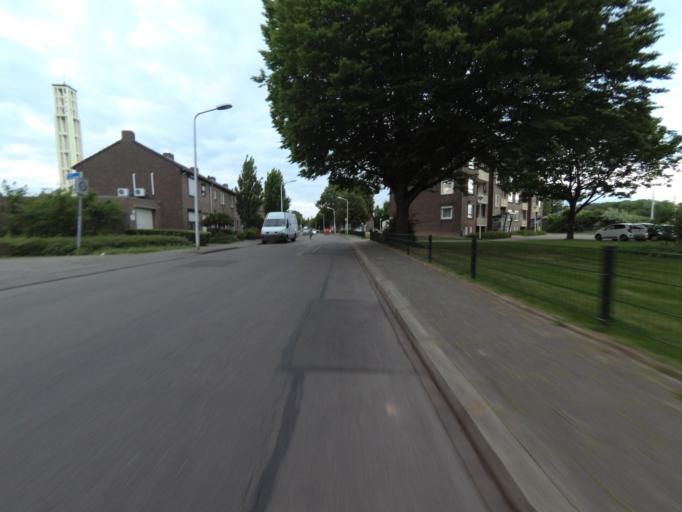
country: NL
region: Limburg
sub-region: Gemeente Maastricht
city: Heer
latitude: 50.8623
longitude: 5.7160
